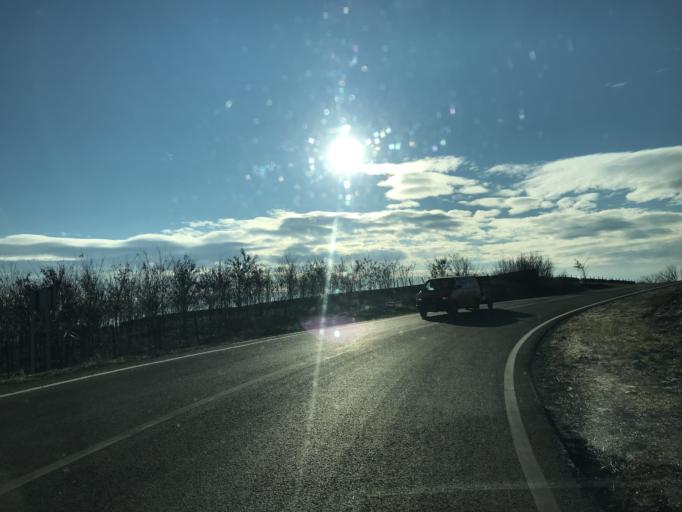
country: RO
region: Olt
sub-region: Comuna Ganeasa
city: Ganeasa
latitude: 44.3955
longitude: 24.2806
